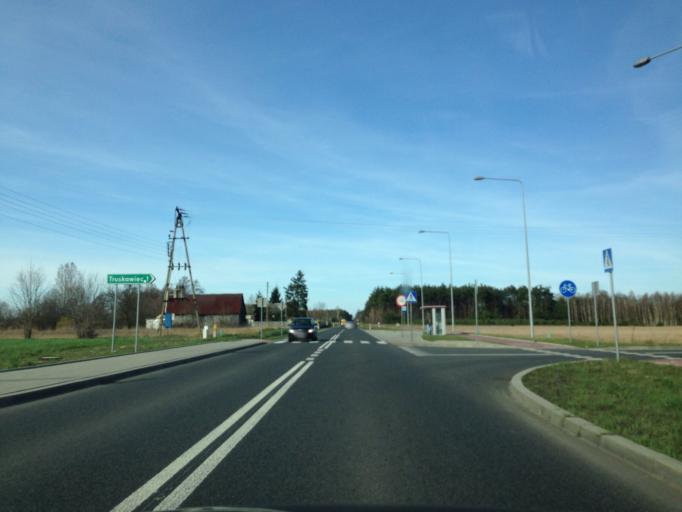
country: PL
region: Lodz Voivodeship
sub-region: Powiat poddebicki
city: Wartkowice
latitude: 51.9474
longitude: 19.0002
